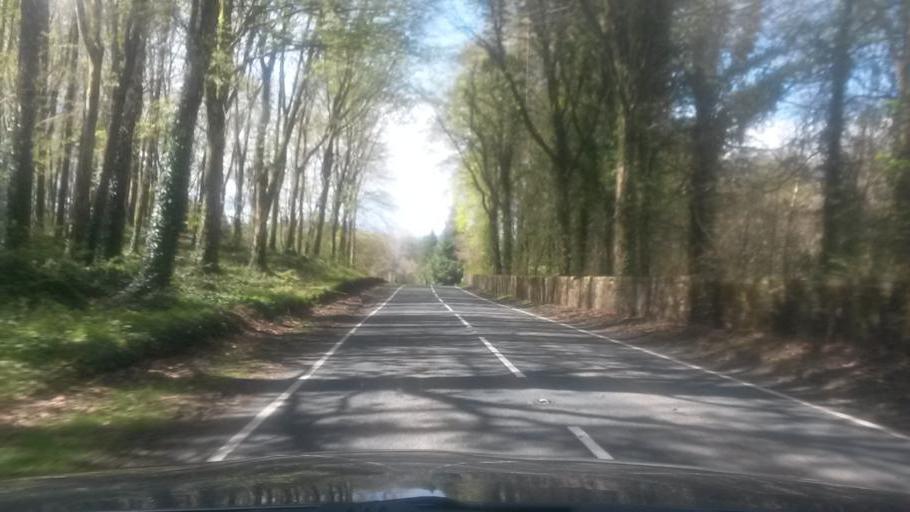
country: GB
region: Northern Ireland
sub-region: Fermanagh District
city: Enniskillen
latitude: 54.3974
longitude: -7.7119
